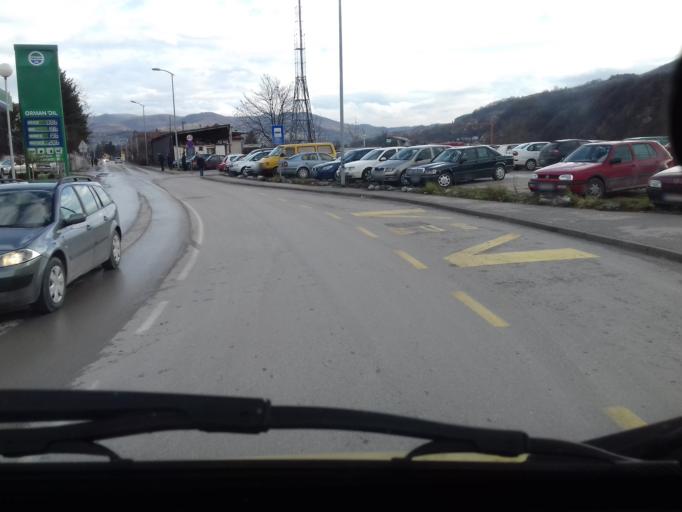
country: BA
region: Federation of Bosnia and Herzegovina
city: Zenica
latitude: 44.1920
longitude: 17.9341
